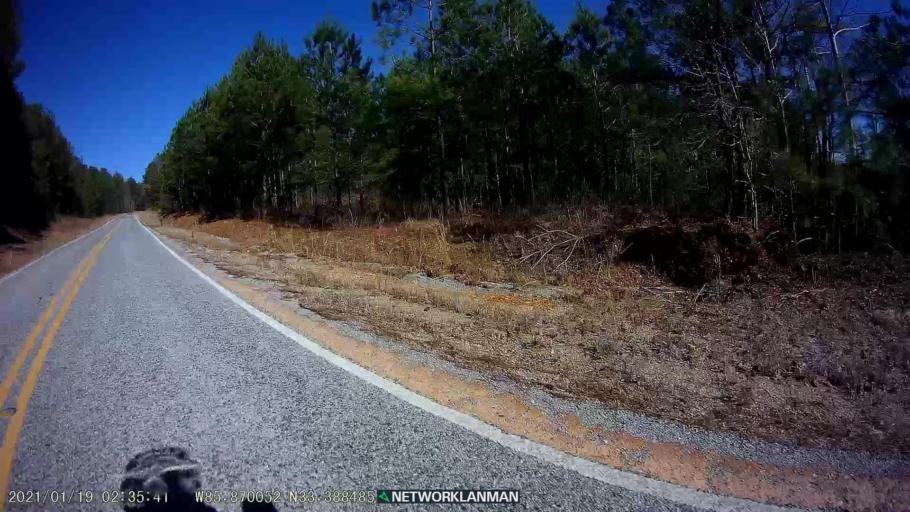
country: US
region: Alabama
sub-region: Clay County
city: Ashland
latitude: 33.3891
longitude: -85.8702
